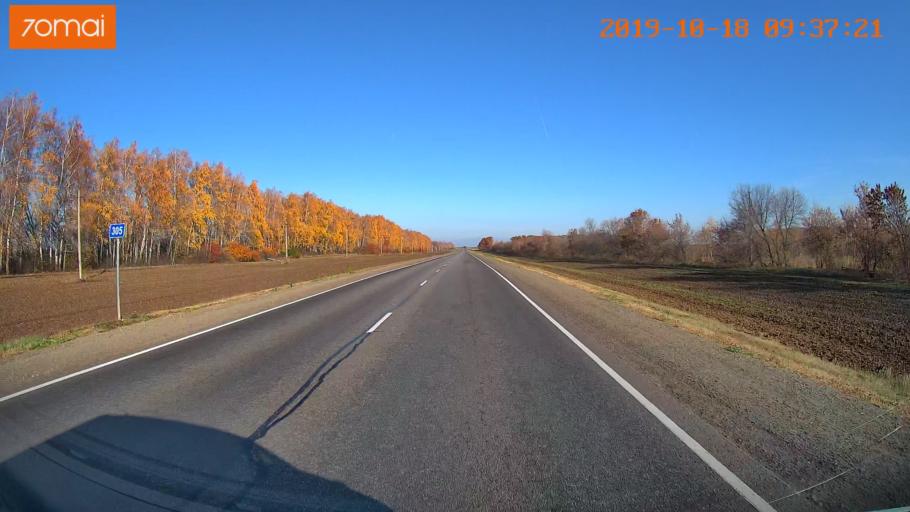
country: RU
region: Tula
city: Yefremov
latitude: 53.2209
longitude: 38.1414
